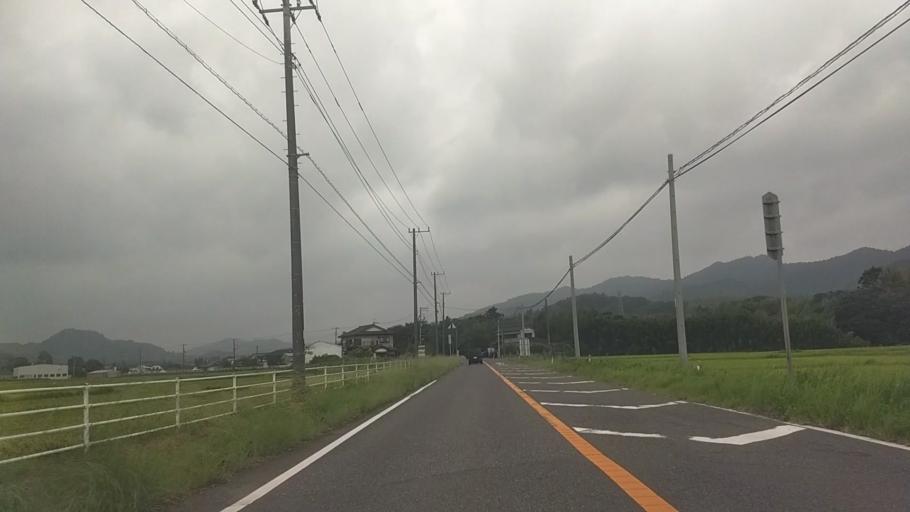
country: JP
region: Chiba
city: Kawaguchi
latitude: 35.1364
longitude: 139.9977
